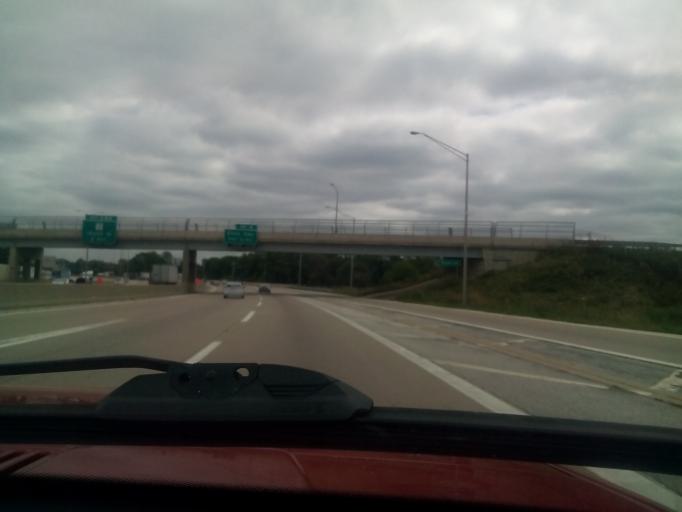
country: US
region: Illinois
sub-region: Cook County
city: University Park
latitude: 41.5795
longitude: -87.6772
